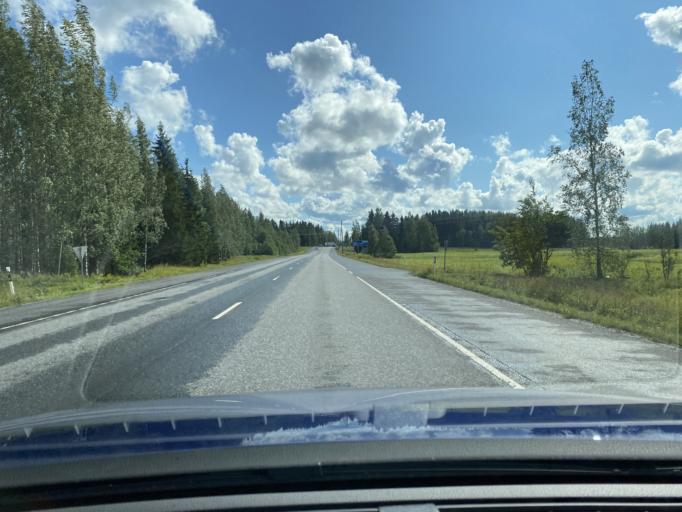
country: FI
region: Pirkanmaa
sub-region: Tampere
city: Lempaeaelae
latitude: 61.3295
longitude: 23.7760
